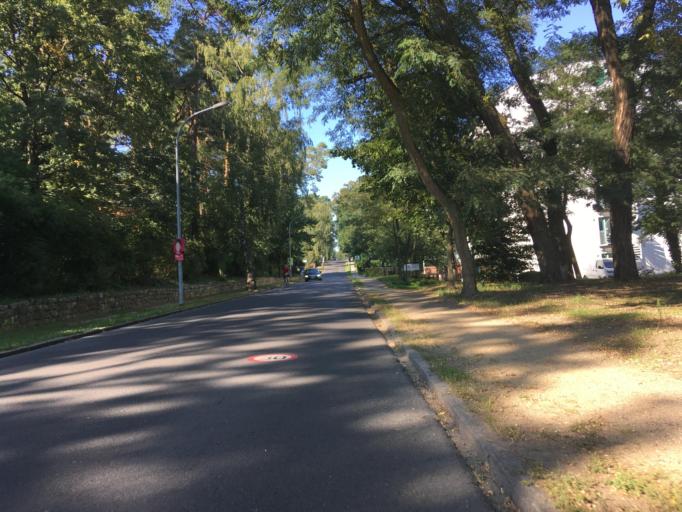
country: DE
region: Brandenburg
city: Wildau
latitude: 52.3311
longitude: 13.6349
